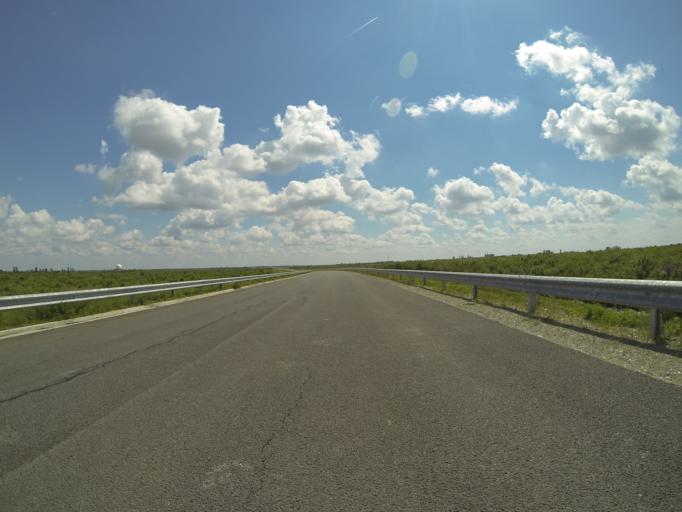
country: RO
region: Dolj
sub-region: Comuna Carcea
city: Carcea
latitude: 44.2845
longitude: 23.9061
